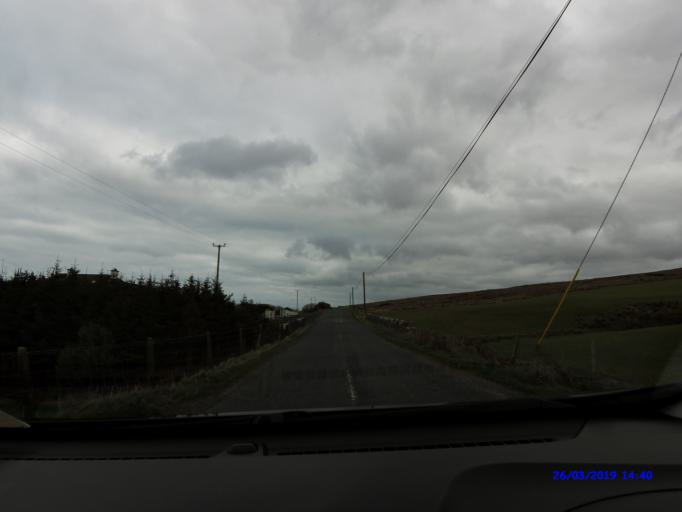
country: IE
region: Connaught
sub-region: Maigh Eo
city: Crossmolina
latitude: 54.3084
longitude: -9.4745
